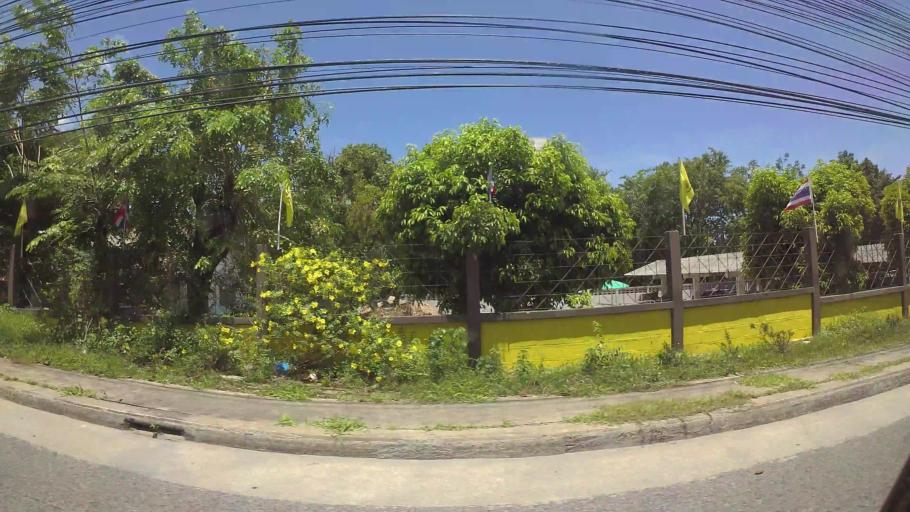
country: TH
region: Chon Buri
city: Si Racha
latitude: 13.1154
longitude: 100.9198
